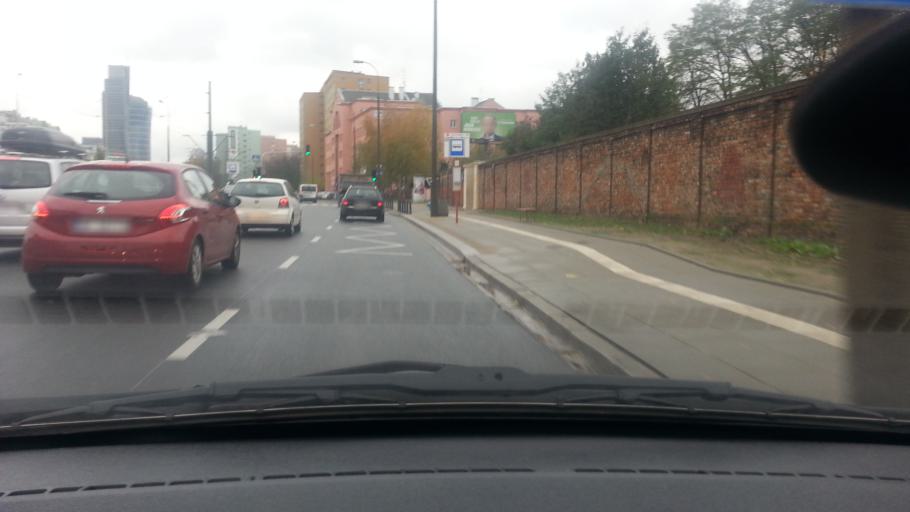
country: PL
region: Masovian Voivodeship
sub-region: Warszawa
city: Wola
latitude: 52.2451
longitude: 20.9769
